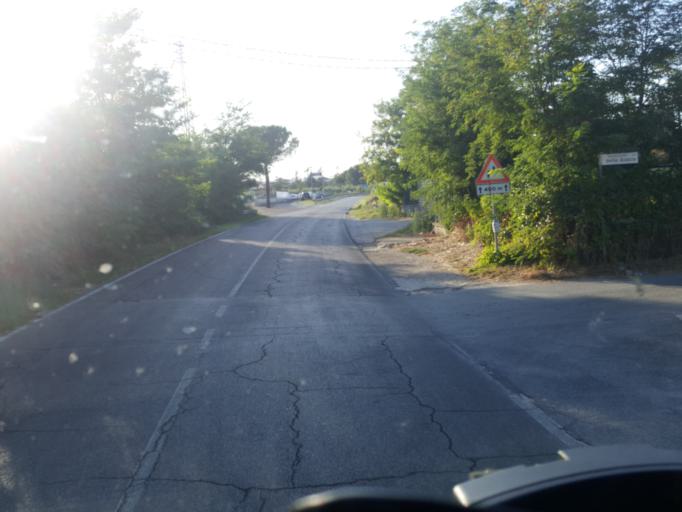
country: IT
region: Latium
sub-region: Citta metropolitana di Roma Capitale
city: Bivio di Capanelle
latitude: 42.1241
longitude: 12.5785
